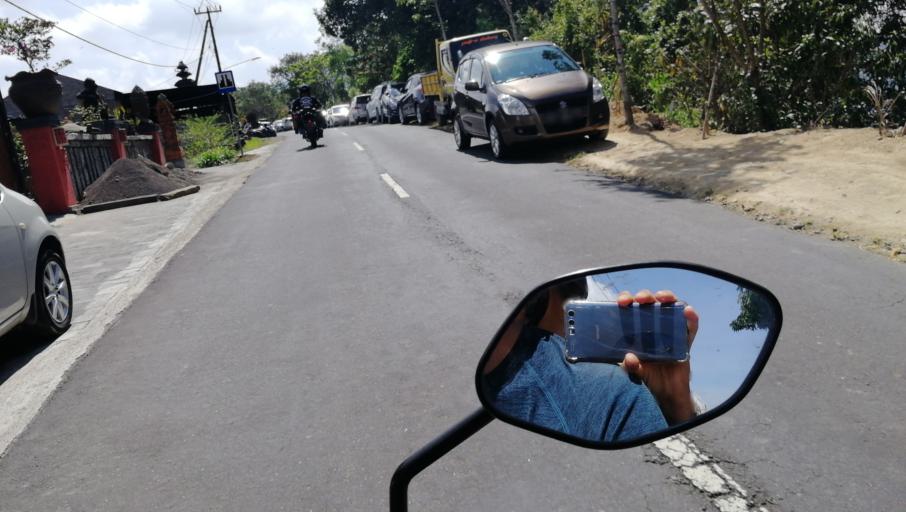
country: ID
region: Bali
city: Munduk
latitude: -8.2380
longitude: 115.1198
